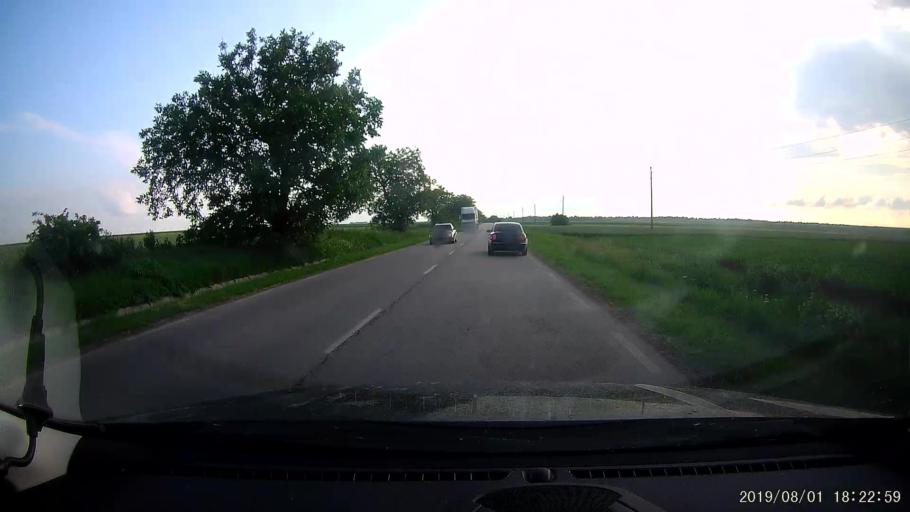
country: BG
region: Shumen
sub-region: Obshtina Kaolinovo
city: Kaolinovo
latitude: 43.6354
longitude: 27.0366
